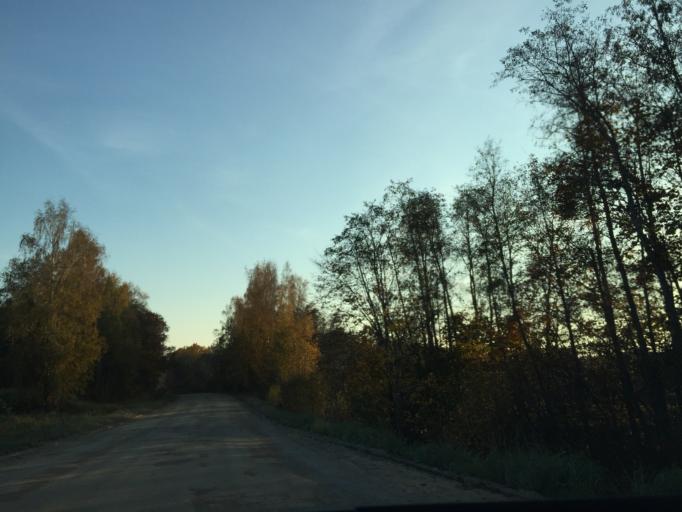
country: LV
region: Vainode
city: Vainode
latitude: 56.5145
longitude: 21.8293
